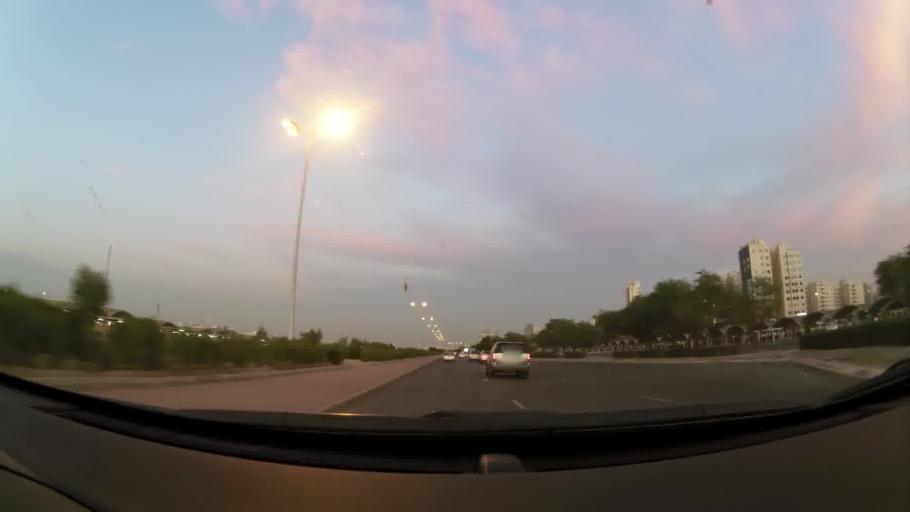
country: KW
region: Al Asimah
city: Ar Rabiyah
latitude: 29.3082
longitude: 47.9089
